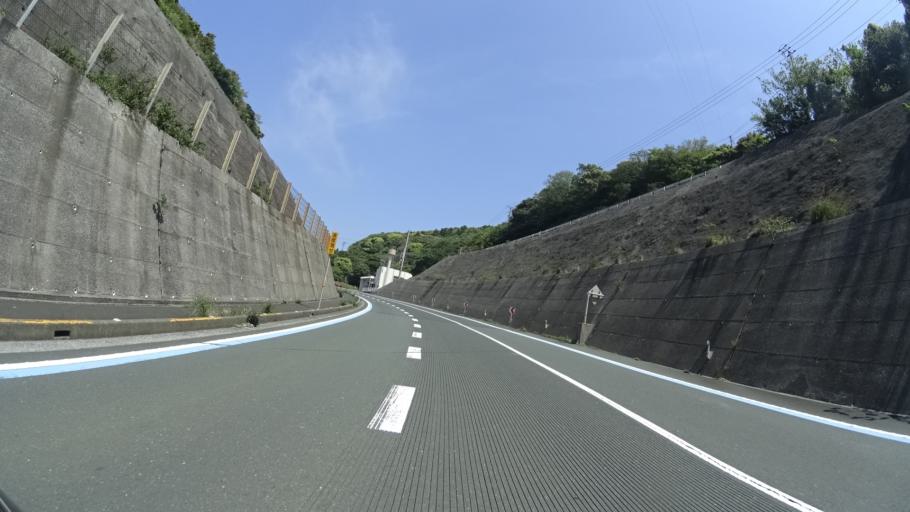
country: JP
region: Ehime
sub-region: Nishiuwa-gun
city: Ikata-cho
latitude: 33.4095
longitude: 132.1732
